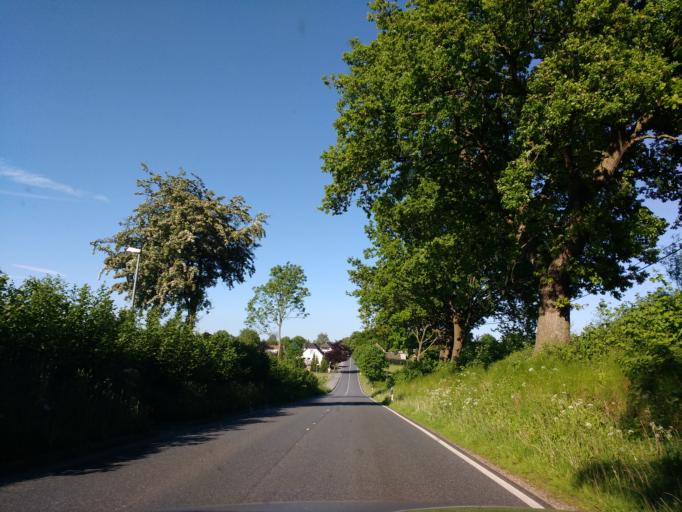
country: DE
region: Mecklenburg-Vorpommern
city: Zurow
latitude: 53.8100
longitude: 11.6160
